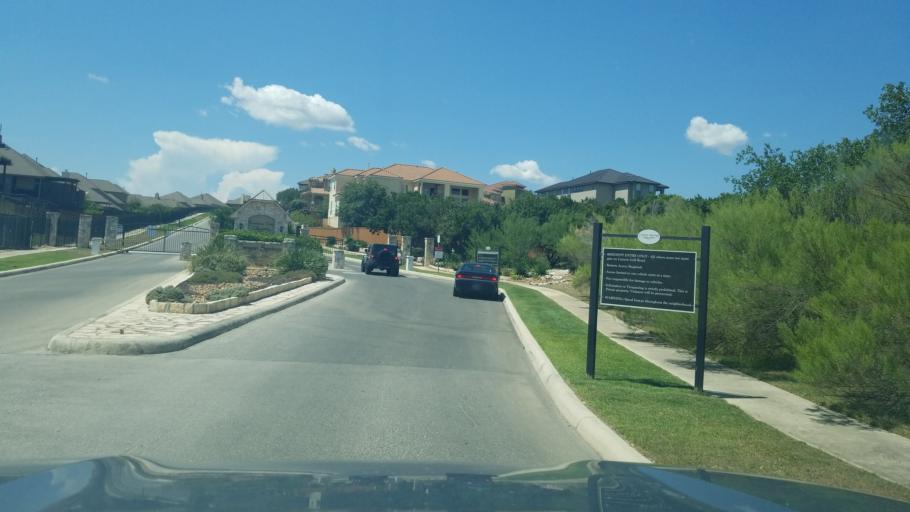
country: US
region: Texas
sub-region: Bexar County
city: Timberwood Park
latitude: 29.6696
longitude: -98.4876
